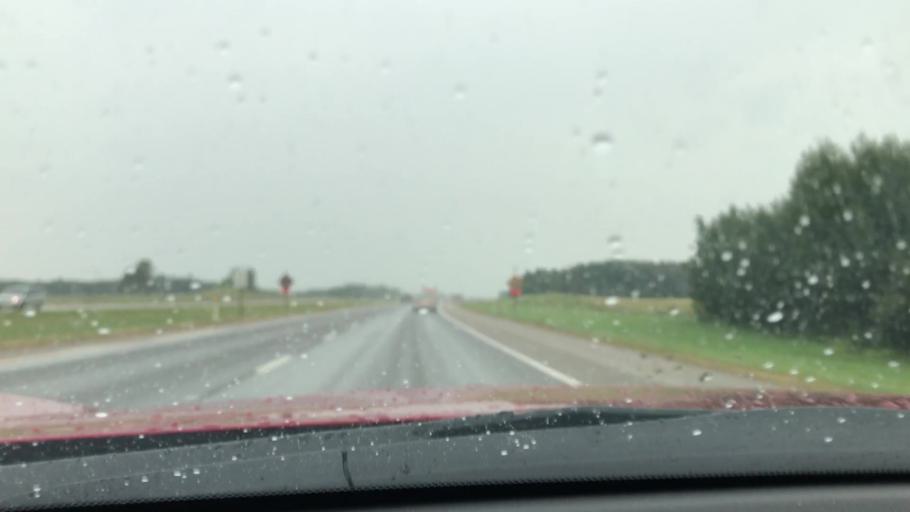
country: CA
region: Alberta
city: Millet
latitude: 52.9424
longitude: -113.6445
